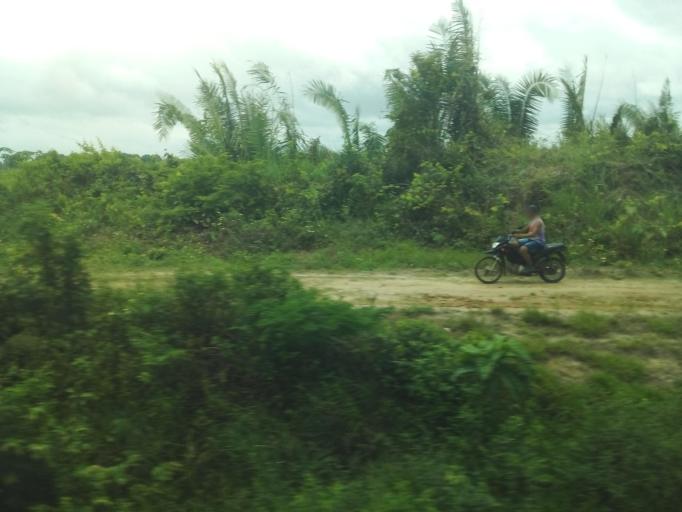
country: BR
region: Maranhao
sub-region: Moncao
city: Moncao
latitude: -3.5825
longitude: -45.0595
